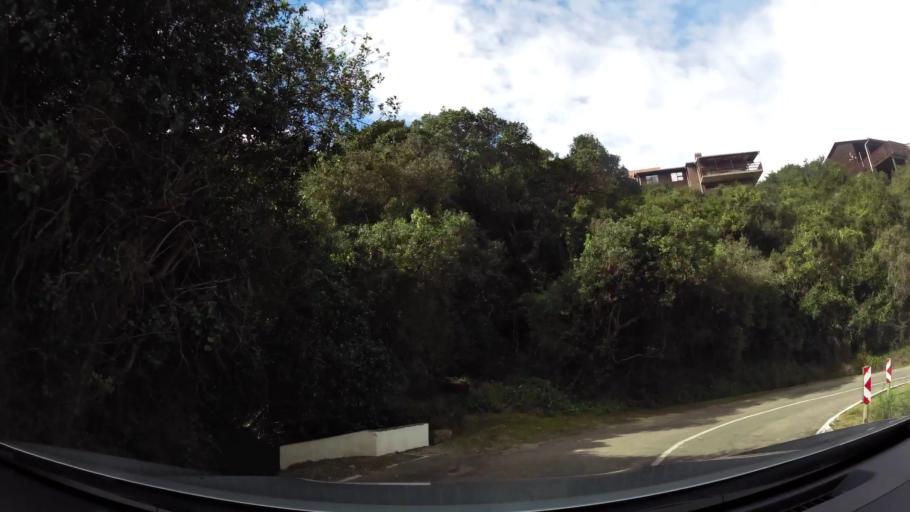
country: ZA
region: Western Cape
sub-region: Eden District Municipality
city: George
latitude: -34.0471
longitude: 22.3169
